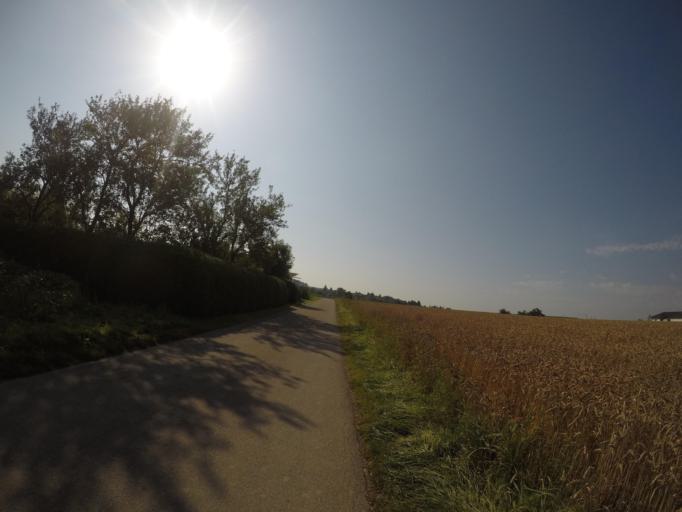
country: DE
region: Baden-Wuerttemberg
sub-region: Tuebingen Region
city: Wain
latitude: 48.1982
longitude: 10.0175
